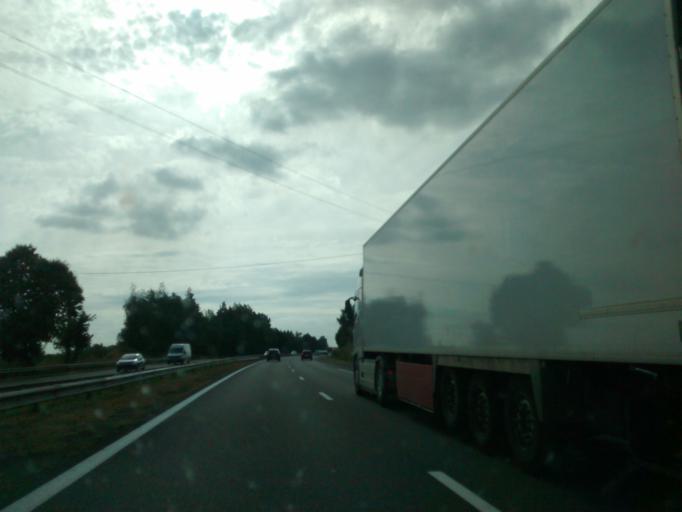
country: FR
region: Brittany
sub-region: Departement d'Ille-et-Vilaine
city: Montauban-de-Bretagne
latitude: 48.1862
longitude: -2.0017
